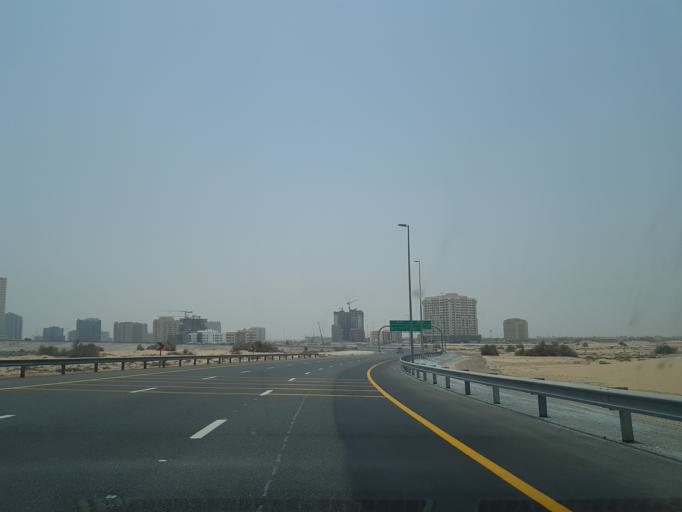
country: AE
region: Dubai
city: Dubai
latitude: 25.1062
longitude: 55.3756
